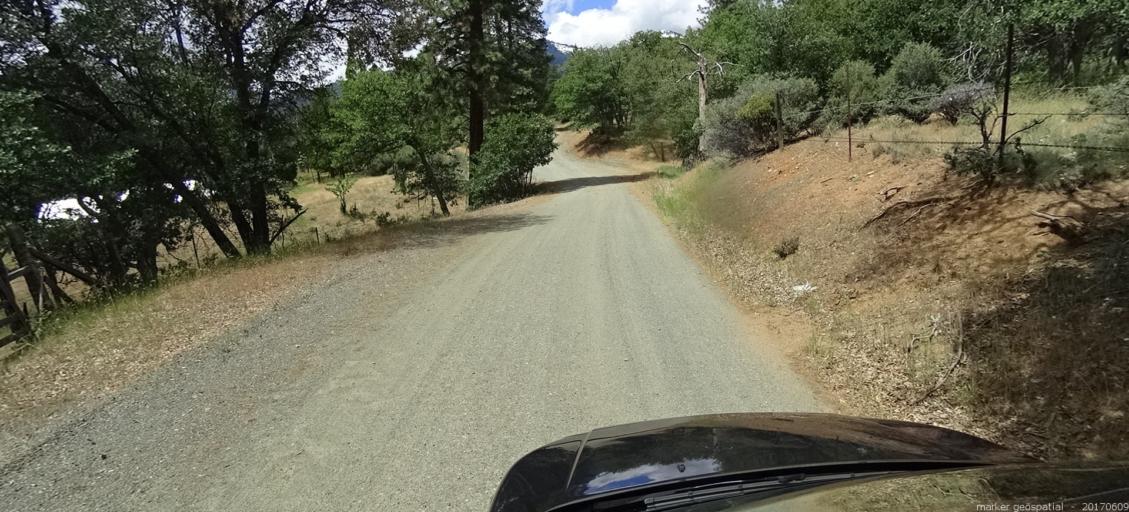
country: US
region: California
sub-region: Siskiyou County
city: Yreka
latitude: 41.3664
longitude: -122.8799
